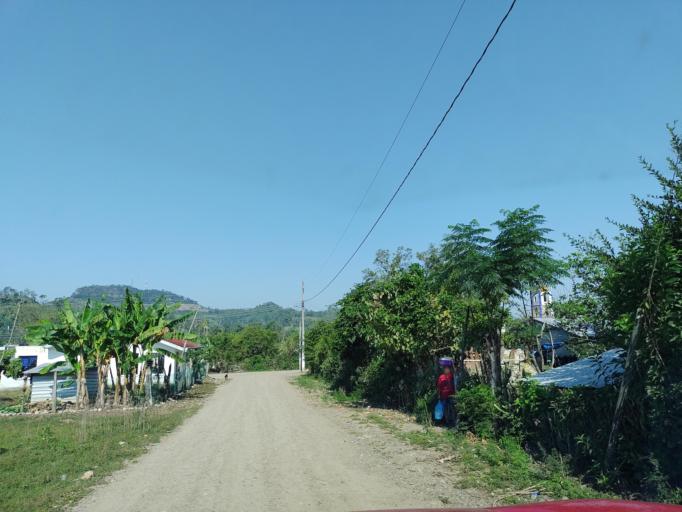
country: MX
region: Veracruz
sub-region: Papantla
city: Polutla
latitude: 20.5163
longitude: -97.2441
